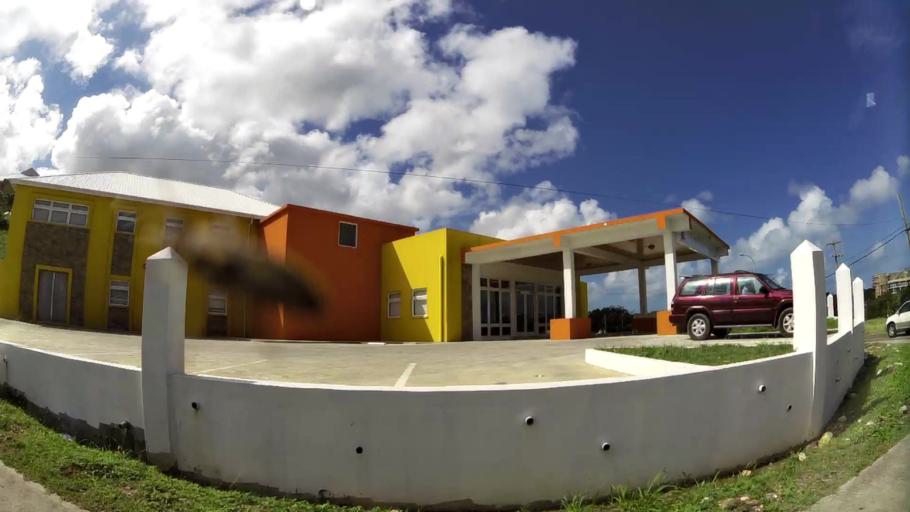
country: AG
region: Saint John
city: Saint John's
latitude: 17.1181
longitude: -61.8381
